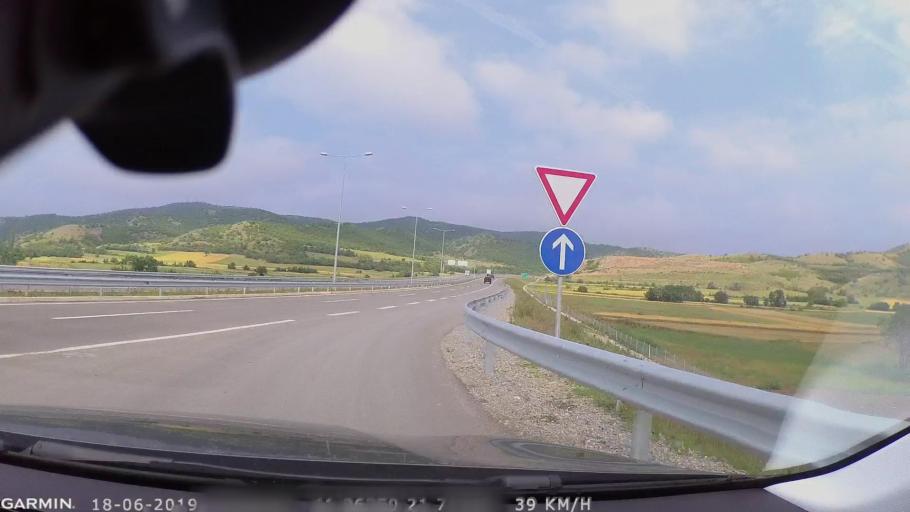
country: MK
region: Petrovec
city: Sredno Konjare
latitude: 41.9463
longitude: 21.8049
